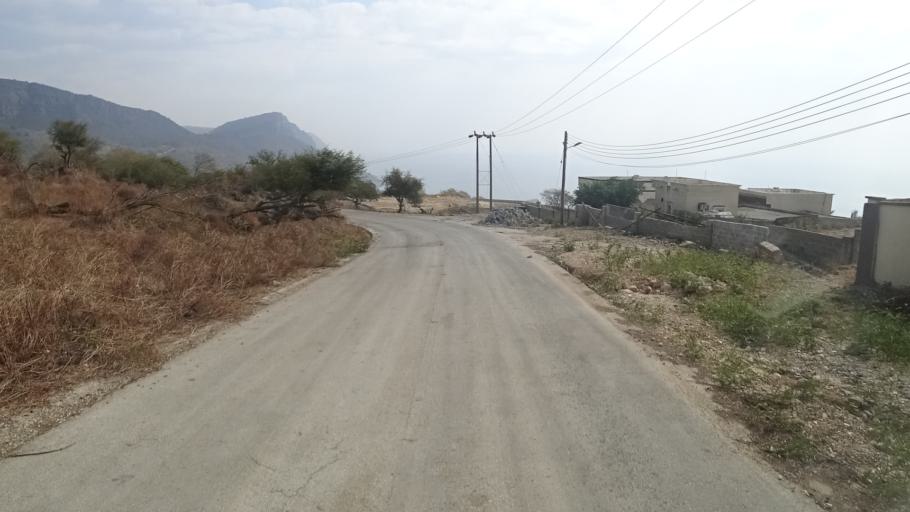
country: YE
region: Al Mahrah
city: Hawf
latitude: 16.7108
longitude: 53.2461
